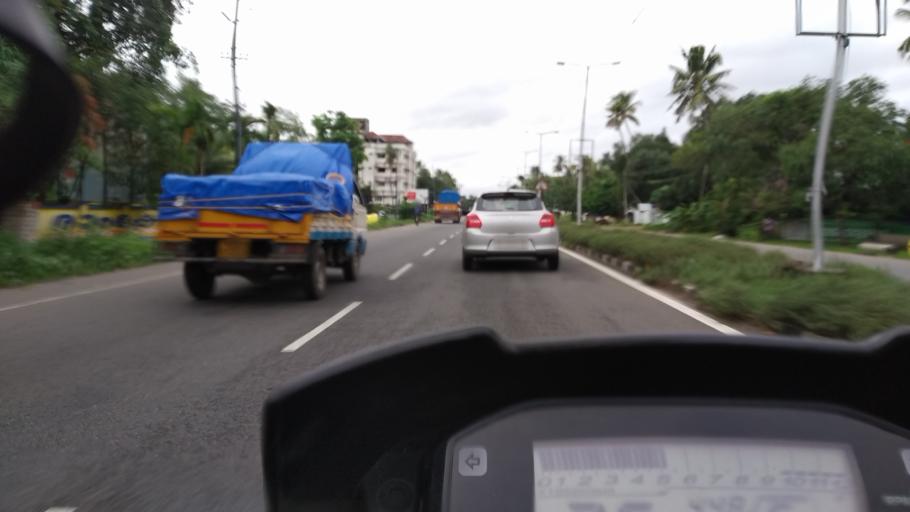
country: IN
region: Kerala
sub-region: Alappuzha
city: Kutiatodu
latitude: 9.8119
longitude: 76.3136
